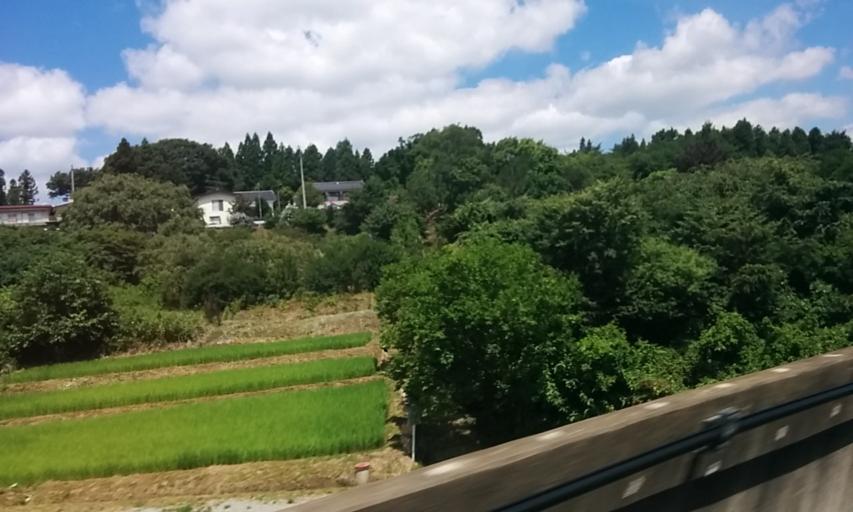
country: JP
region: Fukushima
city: Nihommatsu
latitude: 37.5546
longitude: 140.4529
